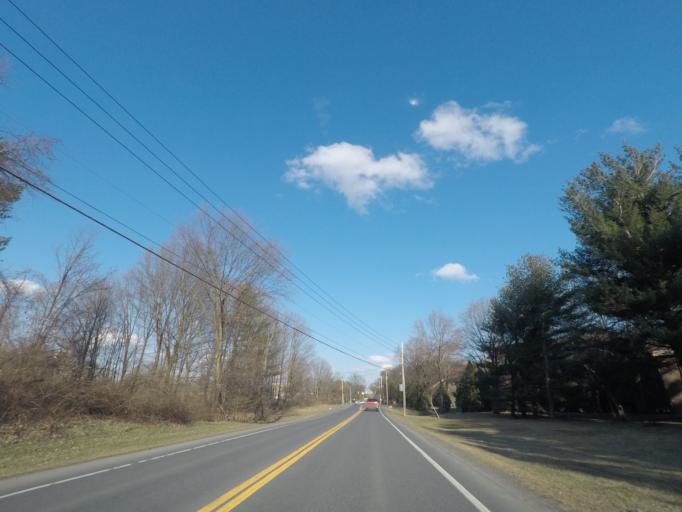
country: US
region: New York
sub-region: Saratoga County
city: Country Knolls
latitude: 42.8553
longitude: -73.7855
